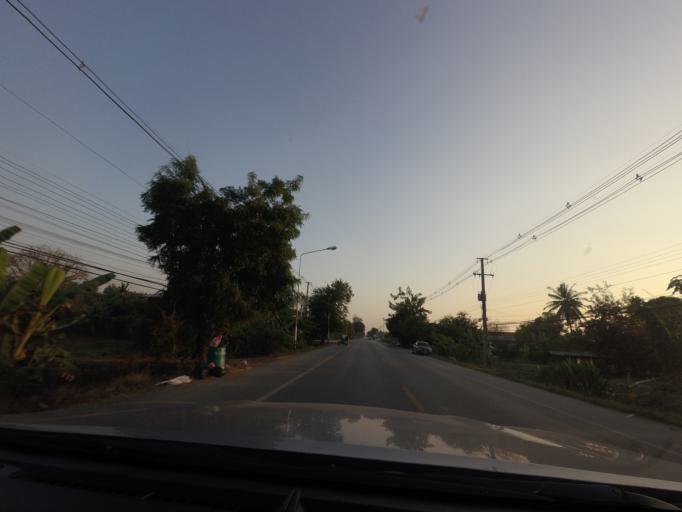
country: TH
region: Sukhothai
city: Si Samrong
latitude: 17.1328
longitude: 99.8502
